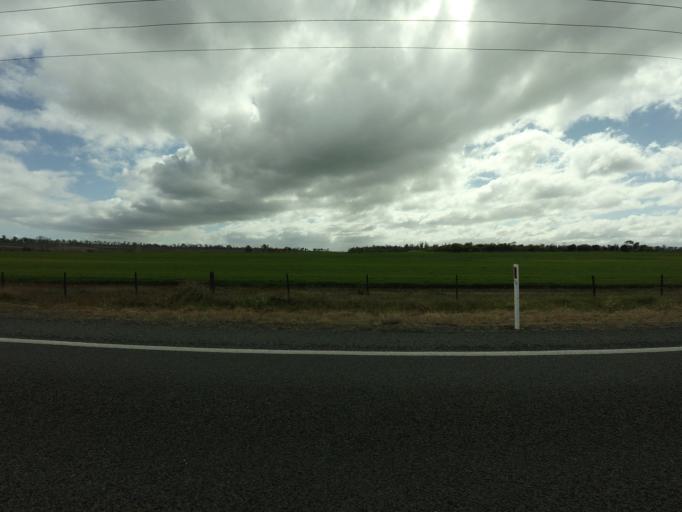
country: AU
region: Tasmania
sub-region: Northern Midlands
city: Evandale
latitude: -41.8346
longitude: 147.4580
